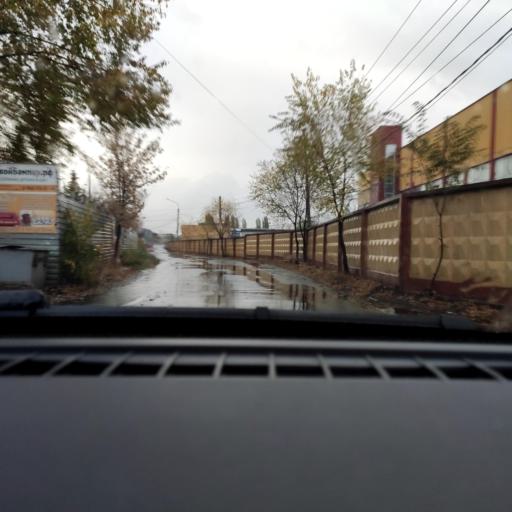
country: RU
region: Voronezj
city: Somovo
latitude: 51.6732
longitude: 39.2952
